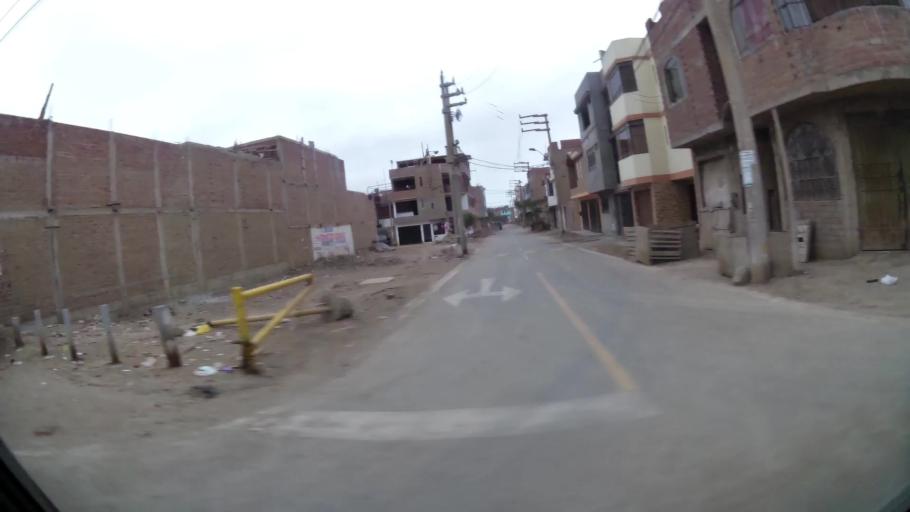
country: PE
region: Lima
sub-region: Lima
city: Independencia
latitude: -11.9787
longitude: -77.0997
